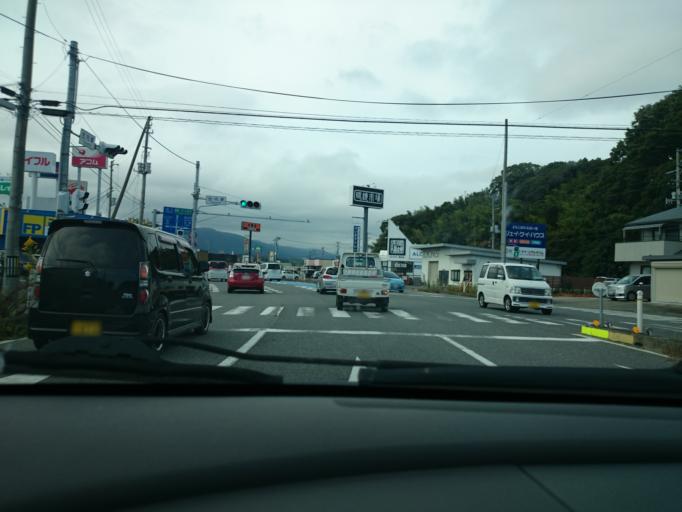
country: JP
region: Fukushima
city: Iwaki
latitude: 36.9866
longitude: 140.8705
